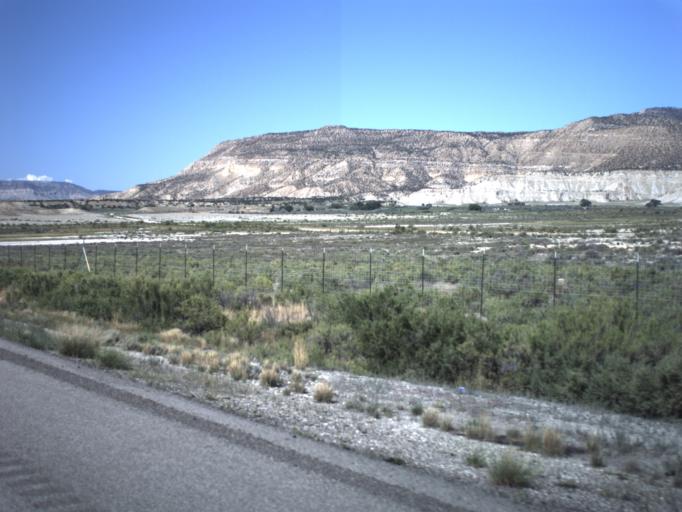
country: US
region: Utah
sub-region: Emery County
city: Ferron
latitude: 38.9450
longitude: -111.2165
